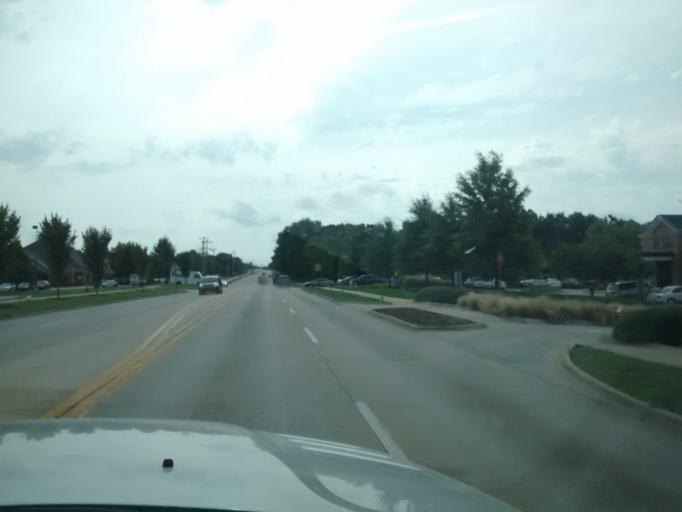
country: US
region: Arkansas
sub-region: Washington County
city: Johnson
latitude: 36.1201
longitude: -94.1376
